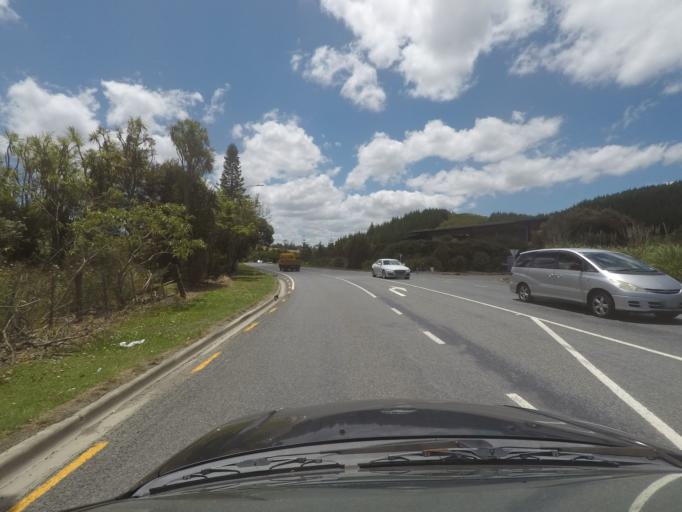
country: NZ
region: Northland
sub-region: Whangarei
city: Whangarei
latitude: -35.7510
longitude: 174.3204
